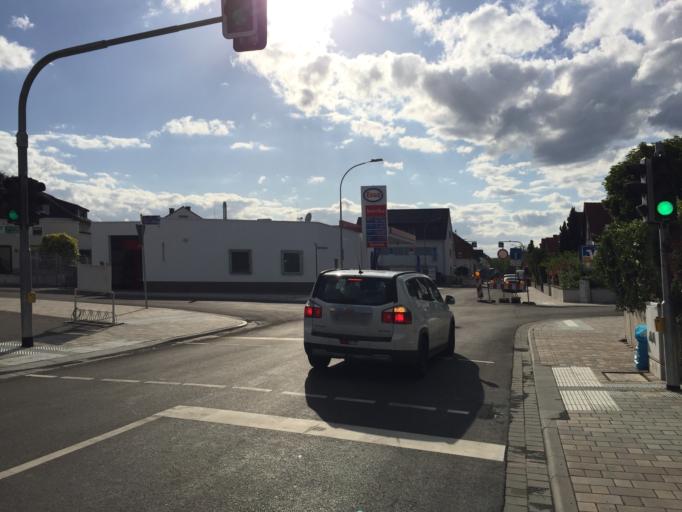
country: DE
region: Hesse
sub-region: Regierungsbezirk Darmstadt
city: Karben
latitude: 50.2308
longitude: 8.7713
